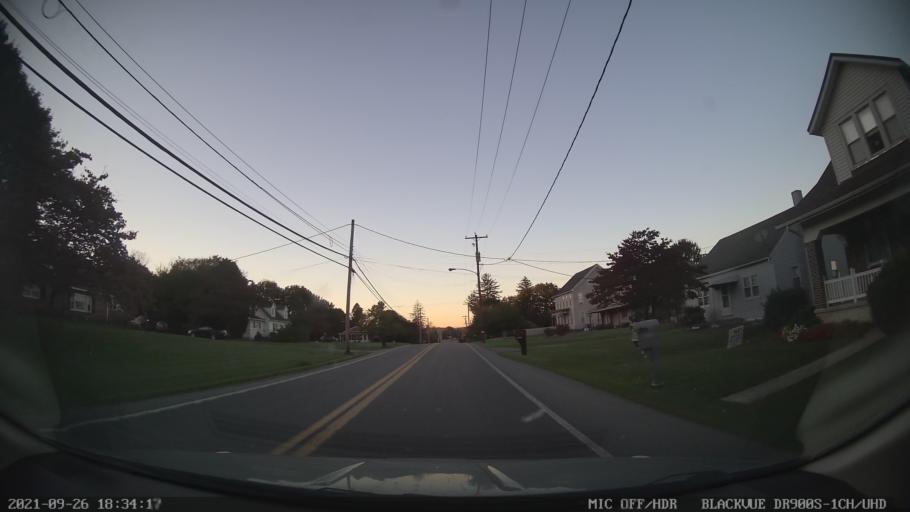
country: US
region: Pennsylvania
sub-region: Berks County
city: Kutztown
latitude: 40.5094
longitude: -75.7715
